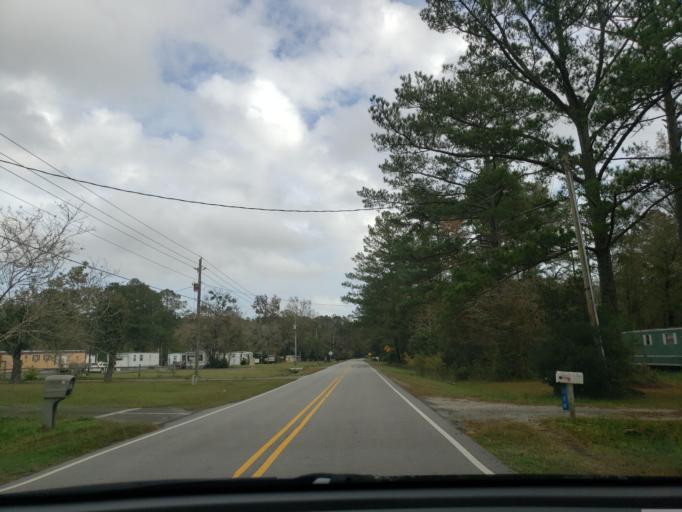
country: US
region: North Carolina
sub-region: Onslow County
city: Jacksonville
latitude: 34.7068
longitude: -77.5779
